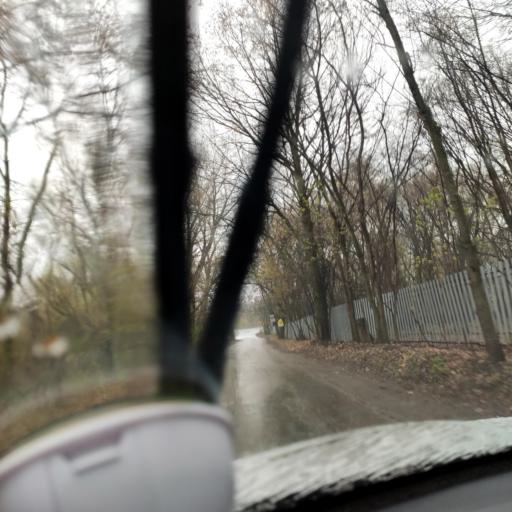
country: RU
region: Samara
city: Novokuybyshevsk
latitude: 53.1390
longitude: 49.9731
